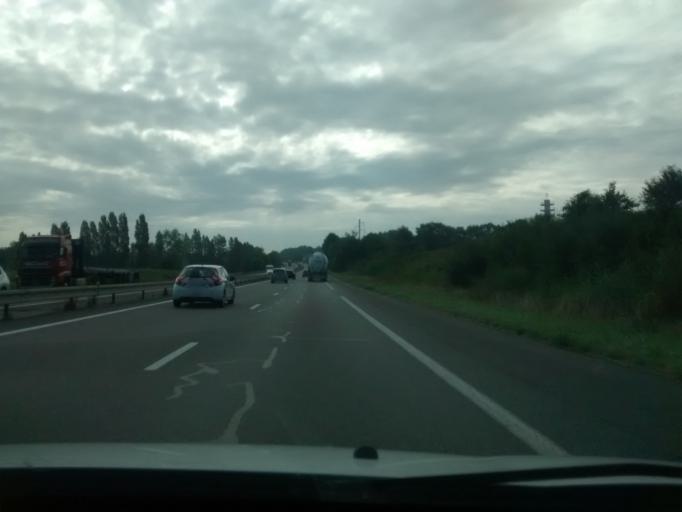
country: FR
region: Pays de la Loire
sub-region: Departement de la Mayenne
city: Saint-Pierre-la-Cour
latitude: 48.0805
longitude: -1.0045
